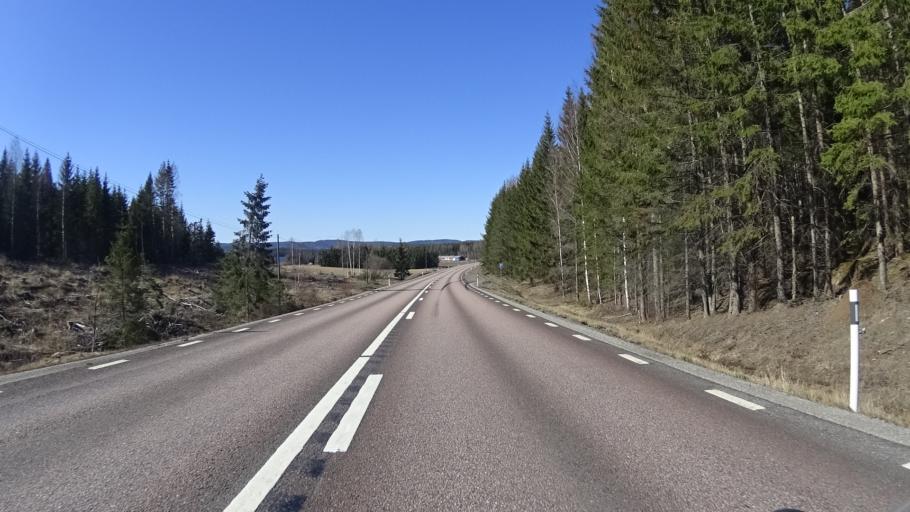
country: SE
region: Vaermland
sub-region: Sunne Kommun
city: Sunne
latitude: 59.6300
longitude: 12.9511
